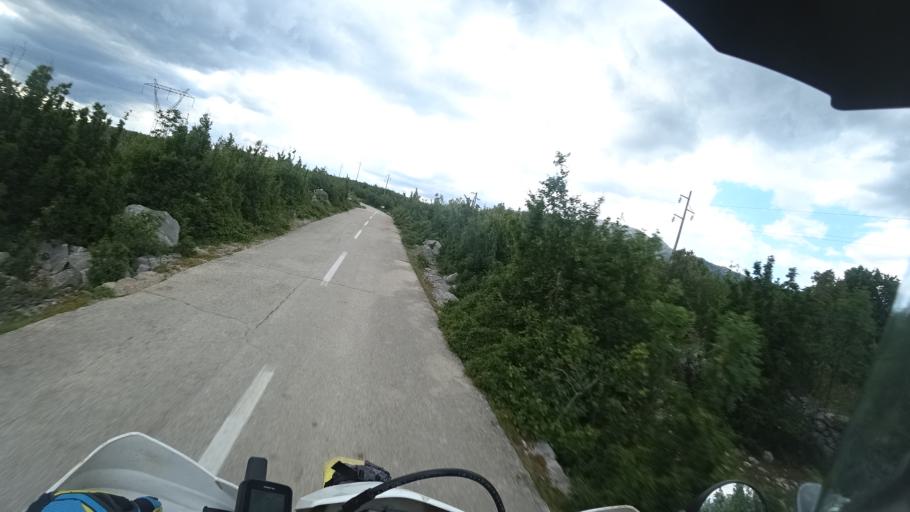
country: HR
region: Zadarska
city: Gracac
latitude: 44.2015
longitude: 15.8628
